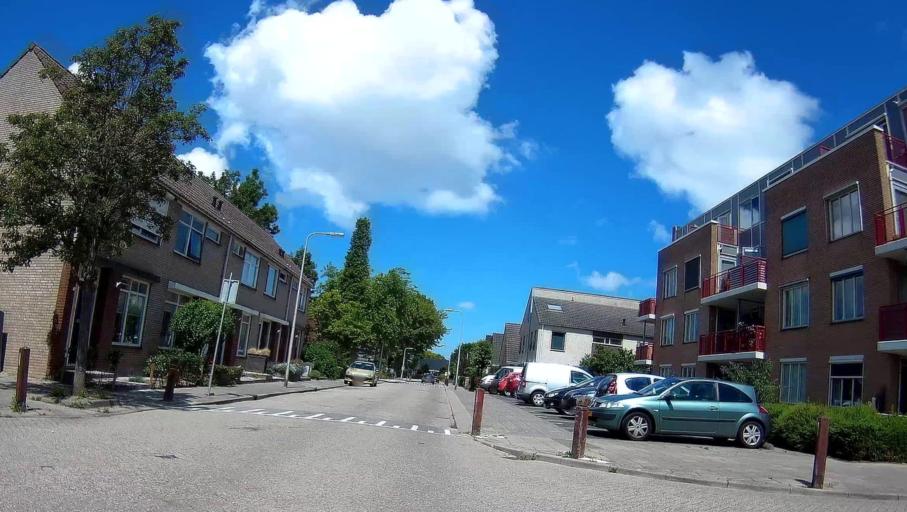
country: NL
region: South Holland
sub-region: Gemeente Westland
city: De Lier
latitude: 51.9801
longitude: 4.2472
